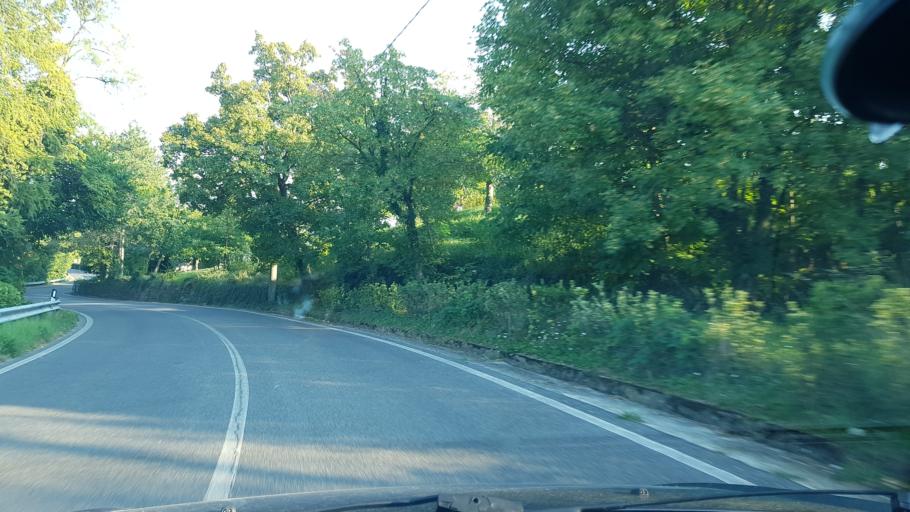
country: IT
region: Friuli Venezia Giulia
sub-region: Provincia di Gorizia
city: San Floriano del Collio
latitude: 45.9841
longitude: 13.5991
